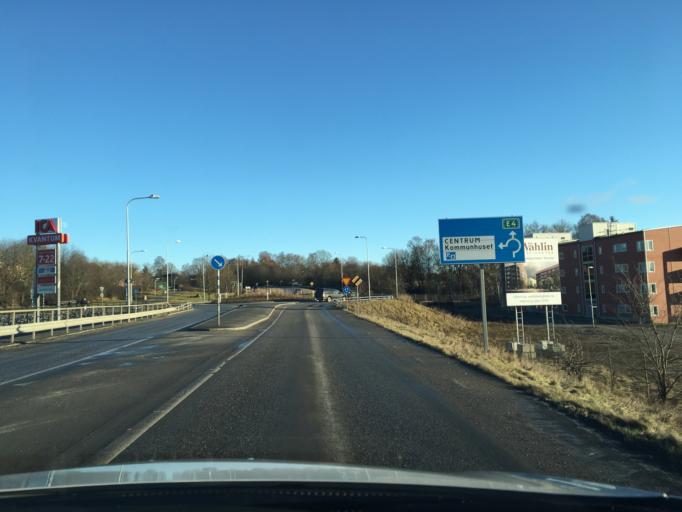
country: SE
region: Uppsala
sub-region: Knivsta Kommun
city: Knivsta
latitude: 59.7299
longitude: 17.7874
